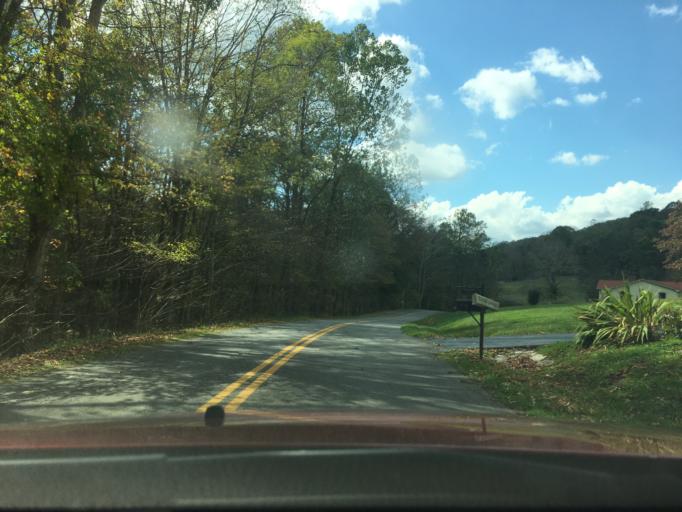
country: US
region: Virginia
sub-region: Giles County
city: Pembroke
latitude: 37.3491
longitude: -80.6040
